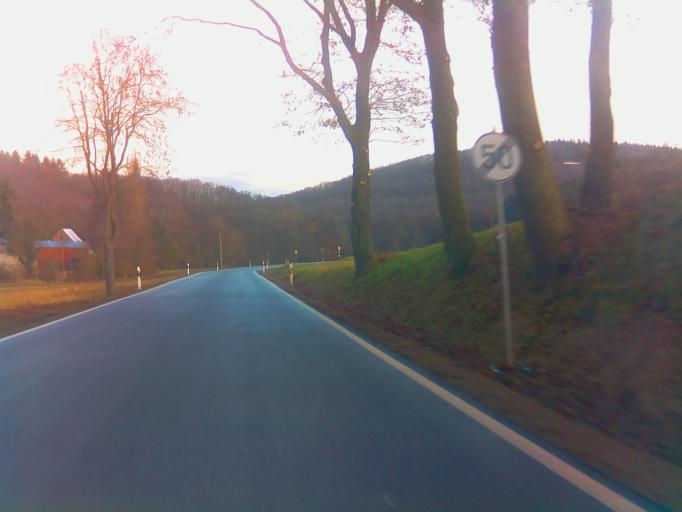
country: DE
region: Rheinland-Pfalz
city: Nieder-Wiesen
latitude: 49.7353
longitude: 7.9775
